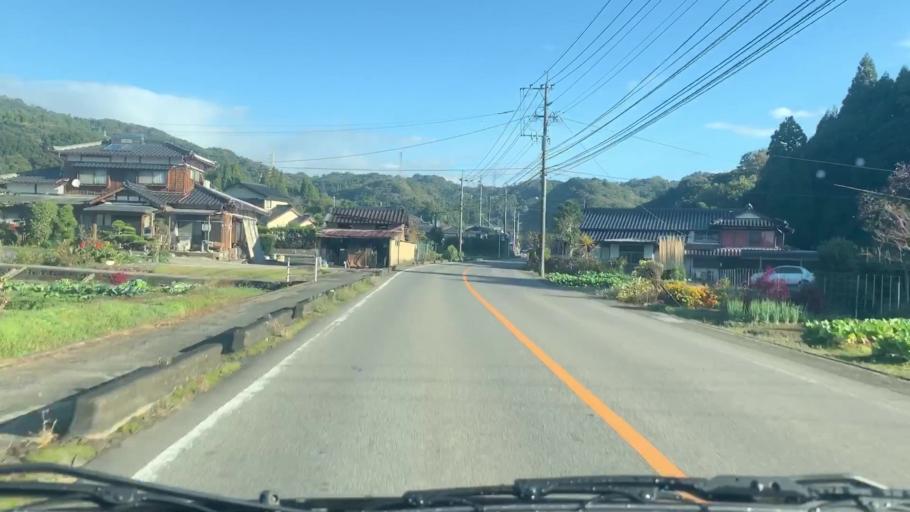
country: JP
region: Saga Prefecture
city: Takeocho-takeo
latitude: 33.2309
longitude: 130.0603
